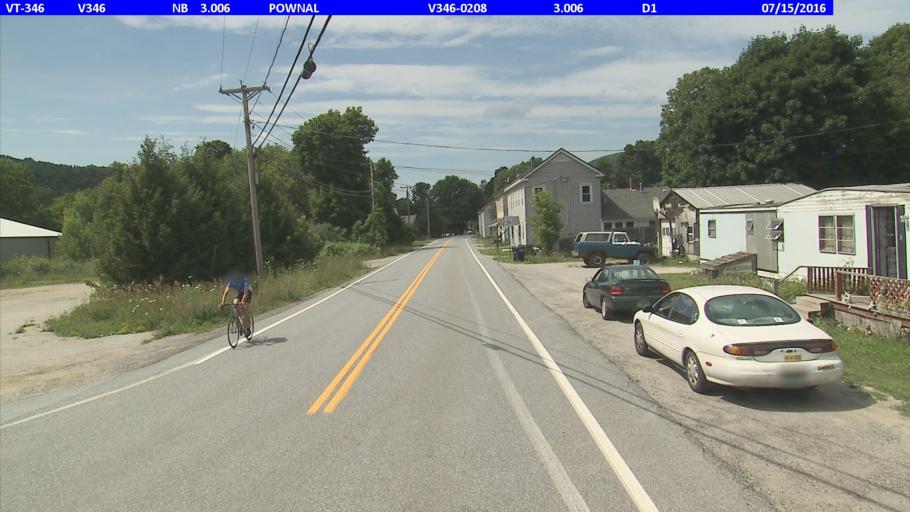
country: US
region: Massachusetts
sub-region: Berkshire County
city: Williamstown
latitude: 42.7977
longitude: -73.2646
